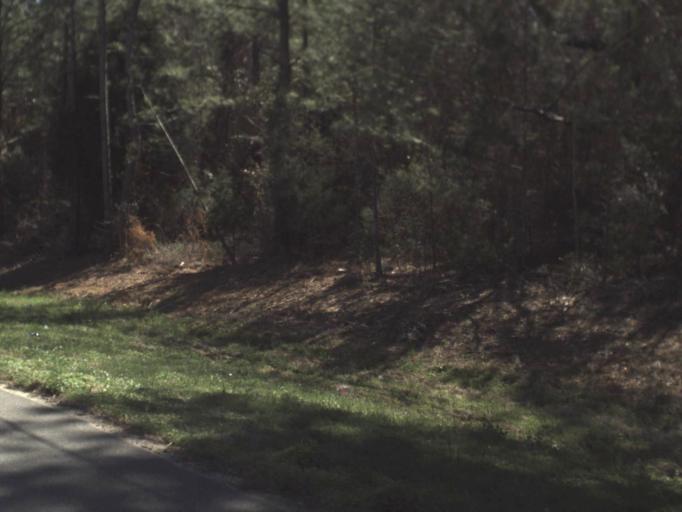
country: US
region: Florida
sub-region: Jackson County
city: Marianna
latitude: 30.7943
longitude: -85.2679
